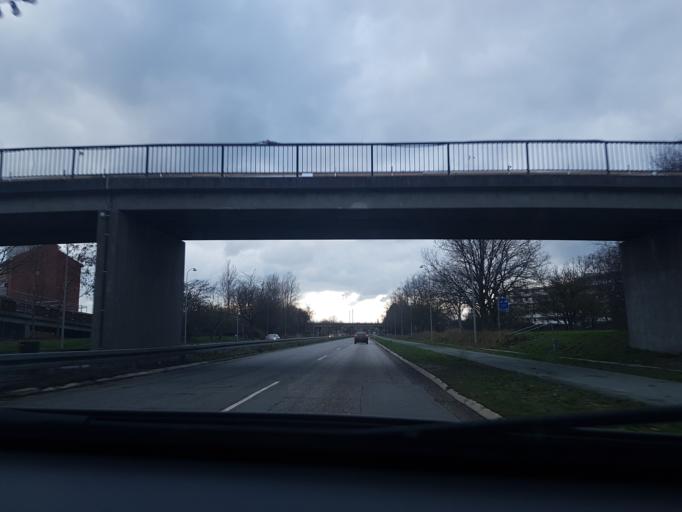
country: DK
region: Capital Region
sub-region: Vallensbaek Kommune
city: Vallensbaek
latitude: 55.6253
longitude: 12.3869
